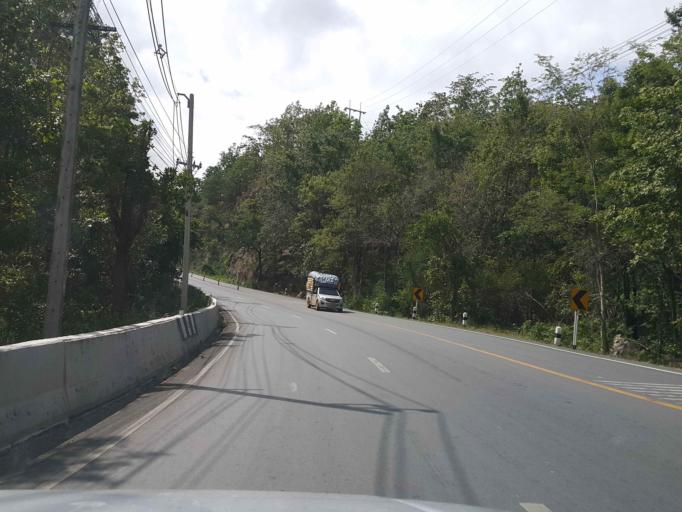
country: TH
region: Tak
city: Tak
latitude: 16.8119
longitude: 98.9786
